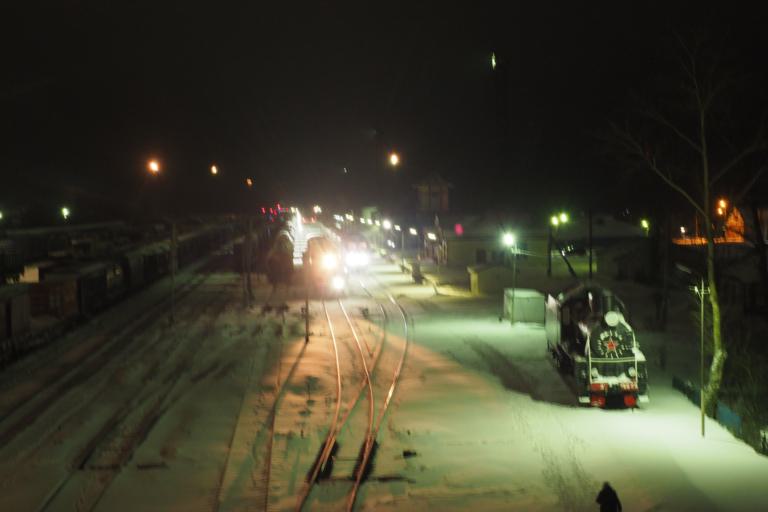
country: RU
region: Tverskaya
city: Sonkovo
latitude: 57.7801
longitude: 37.1656
